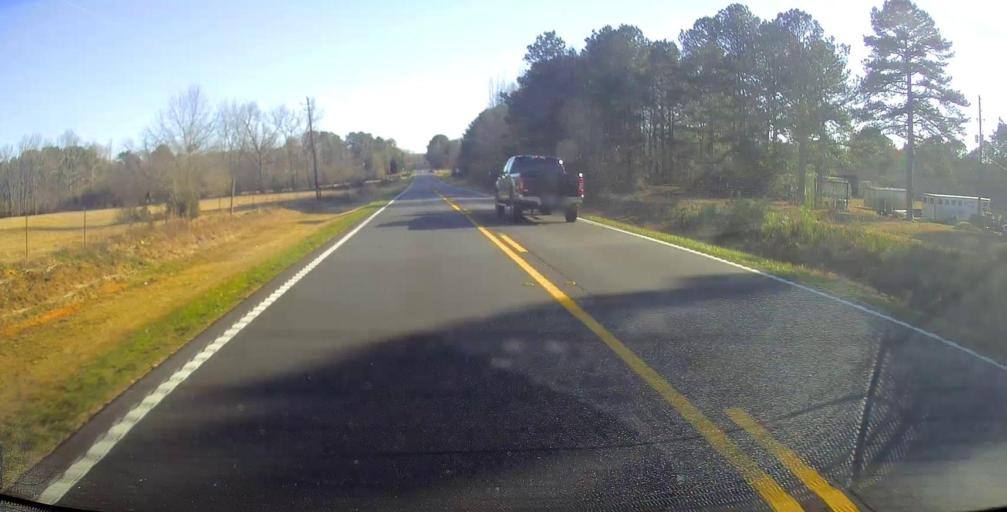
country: US
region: Georgia
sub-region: Talbot County
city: Sardis
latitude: 32.8160
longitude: -84.6977
